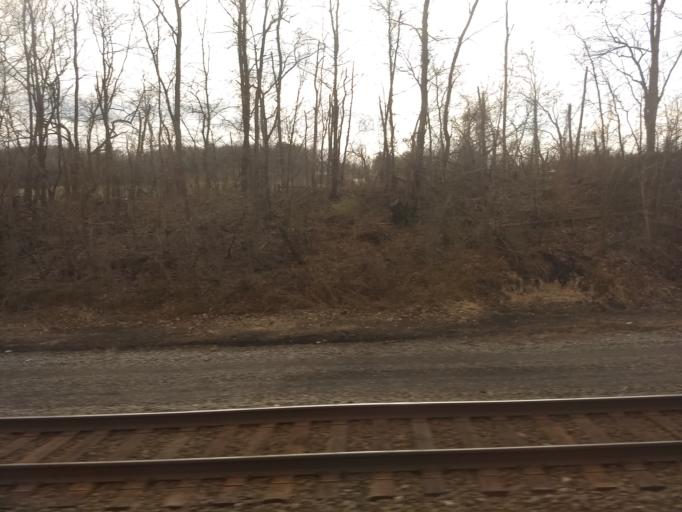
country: US
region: Pennsylvania
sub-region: Mifflin County
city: Belleville
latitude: 40.4999
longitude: -77.7282
